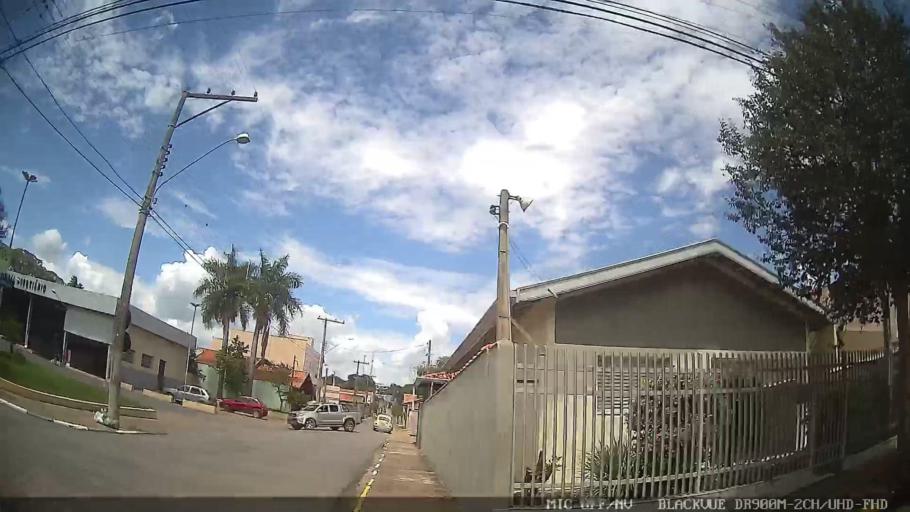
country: BR
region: Sao Paulo
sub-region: Conchas
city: Conchas
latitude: -23.0754
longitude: -47.9758
